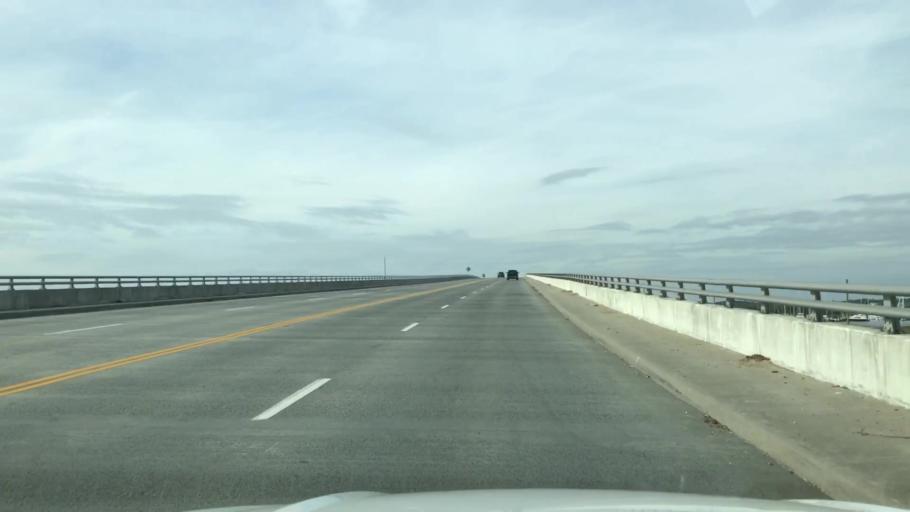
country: US
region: South Carolina
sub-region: Charleston County
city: Charleston
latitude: 32.7532
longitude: -80.0055
